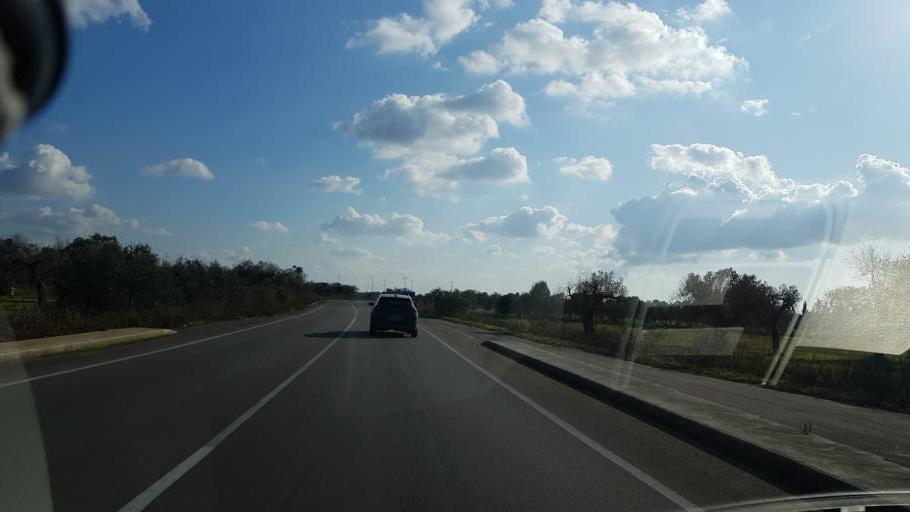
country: IT
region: Apulia
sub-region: Provincia di Lecce
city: Veglie
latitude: 40.3388
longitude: 17.9802
